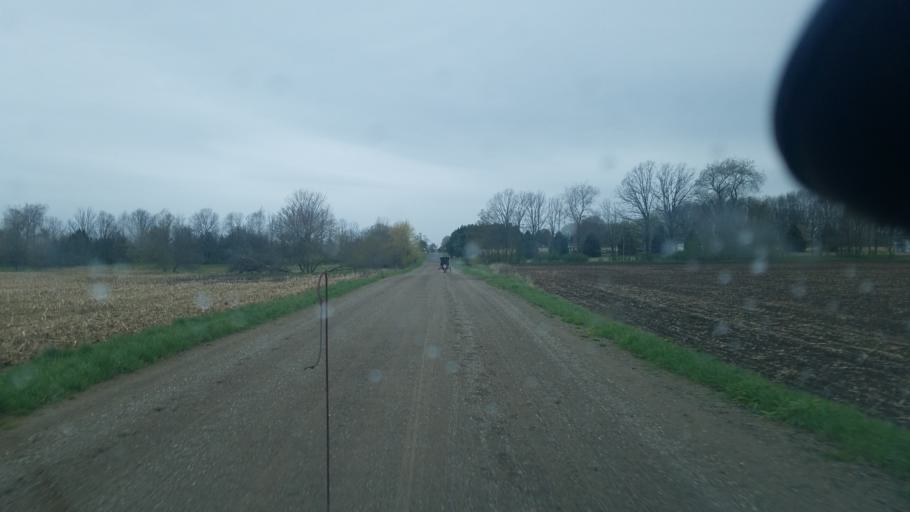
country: US
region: Michigan
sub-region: Montcalm County
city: Lakeview
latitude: 43.5110
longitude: -85.2773
